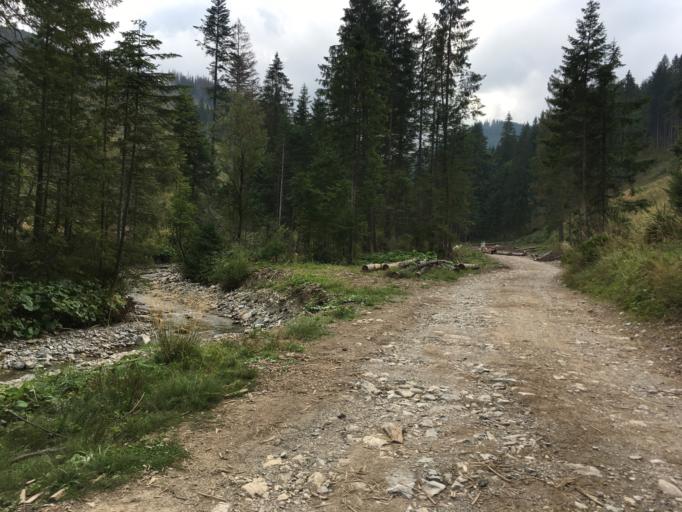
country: PL
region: Lesser Poland Voivodeship
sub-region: Powiat tatrzanski
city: Koscielisko
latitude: 49.2759
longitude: 19.8486
